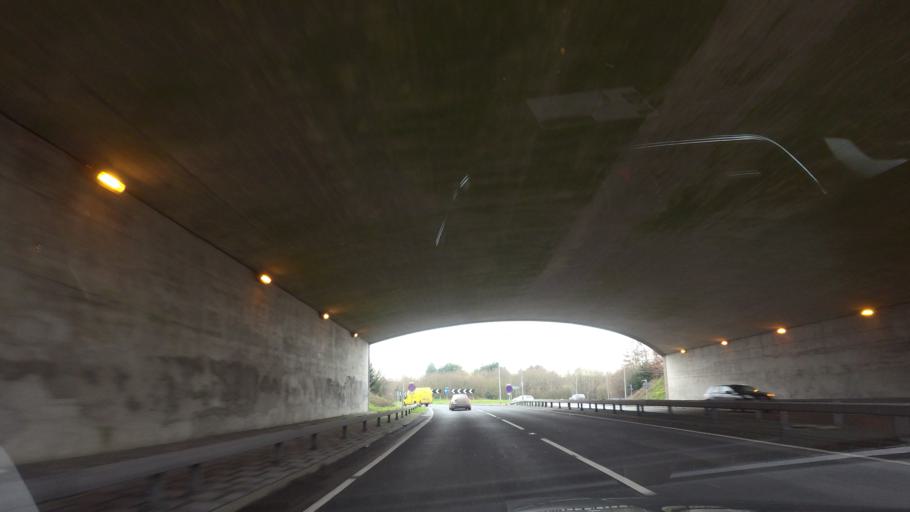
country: GB
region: England
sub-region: East Sussex
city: Wadhurst
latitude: 51.0920
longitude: 0.3963
